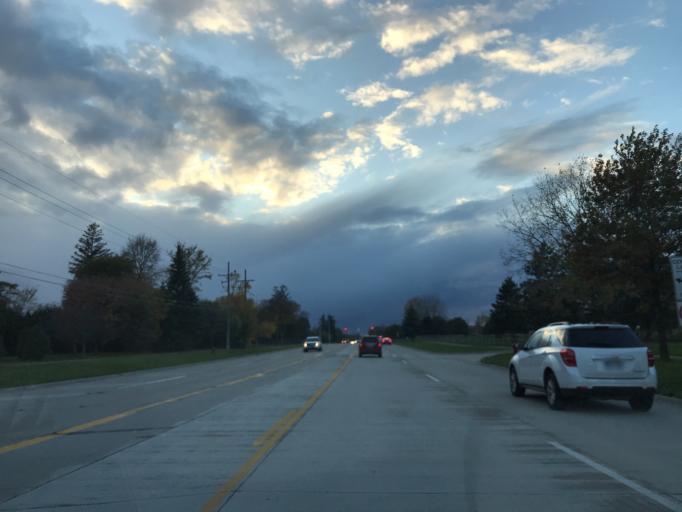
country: US
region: Michigan
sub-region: Oakland County
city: Farmington
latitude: 42.4401
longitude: -83.3937
